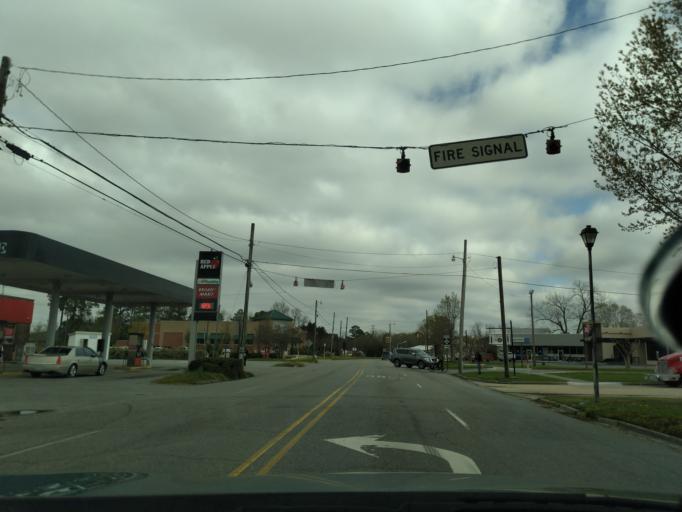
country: US
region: North Carolina
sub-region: Chowan County
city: Edenton
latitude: 36.0681
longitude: -76.6060
